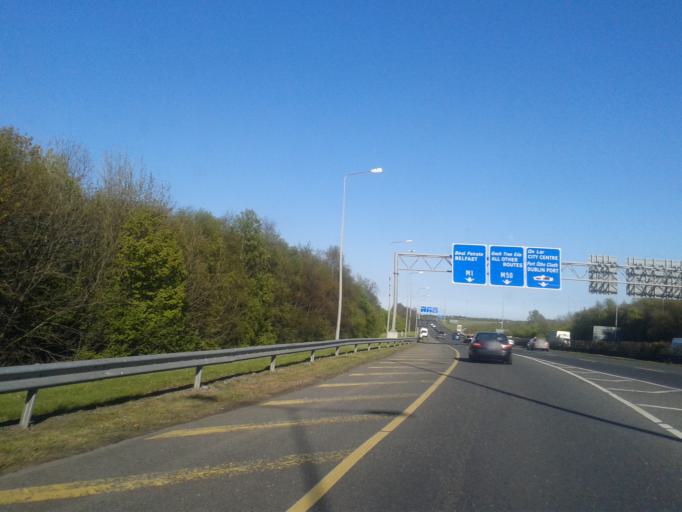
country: IE
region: Leinster
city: Kinsealy-Drinan
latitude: 53.4283
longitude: -6.2272
